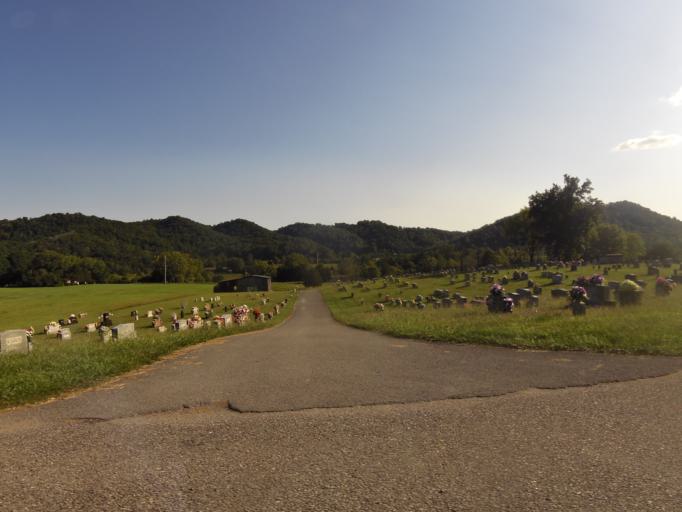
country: US
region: Tennessee
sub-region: Union County
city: Maynardville
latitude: 36.2618
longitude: -83.7742
